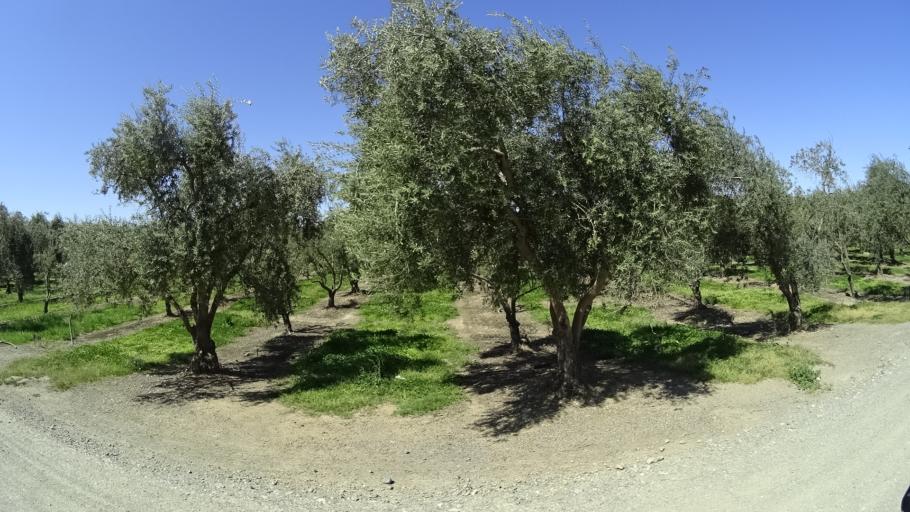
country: US
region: California
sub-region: Glenn County
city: Orland
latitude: 39.6868
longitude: -122.1592
